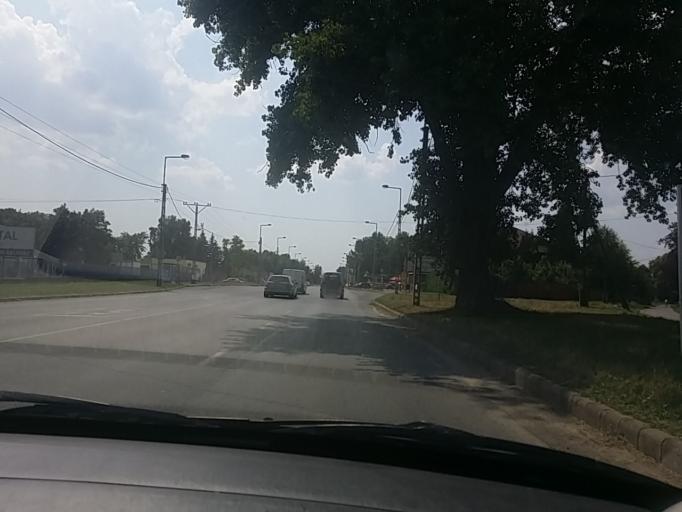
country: HU
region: Tolna
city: Dombovar
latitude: 46.3952
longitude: 18.1472
